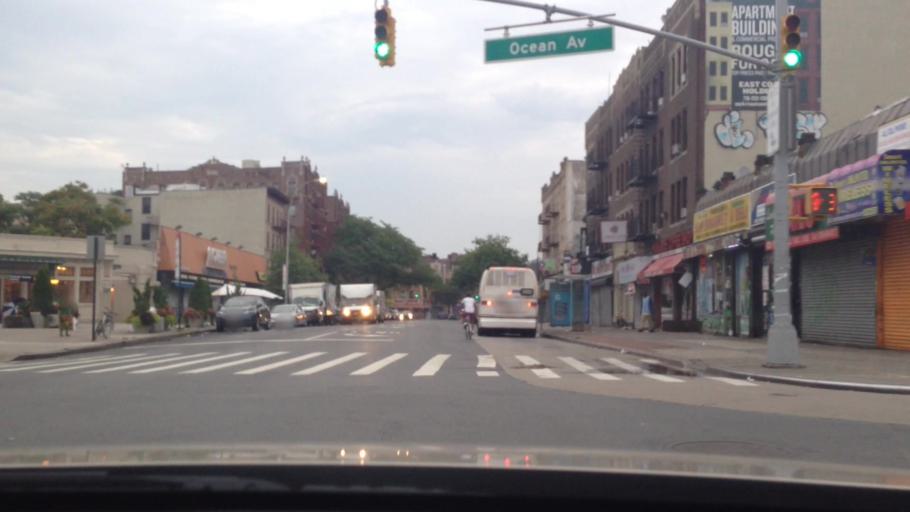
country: US
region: New York
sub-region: Kings County
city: Brooklyn
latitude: 40.6548
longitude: -73.9619
